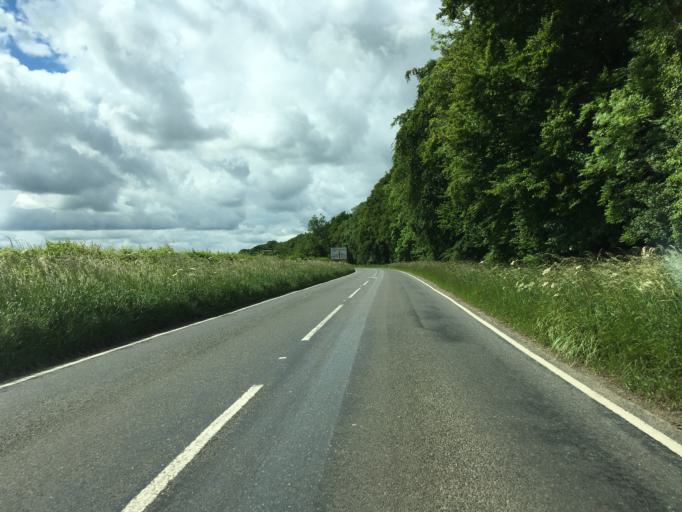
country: GB
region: England
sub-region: Oxfordshire
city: Chipping Norton
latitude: 51.9101
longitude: -1.5539
